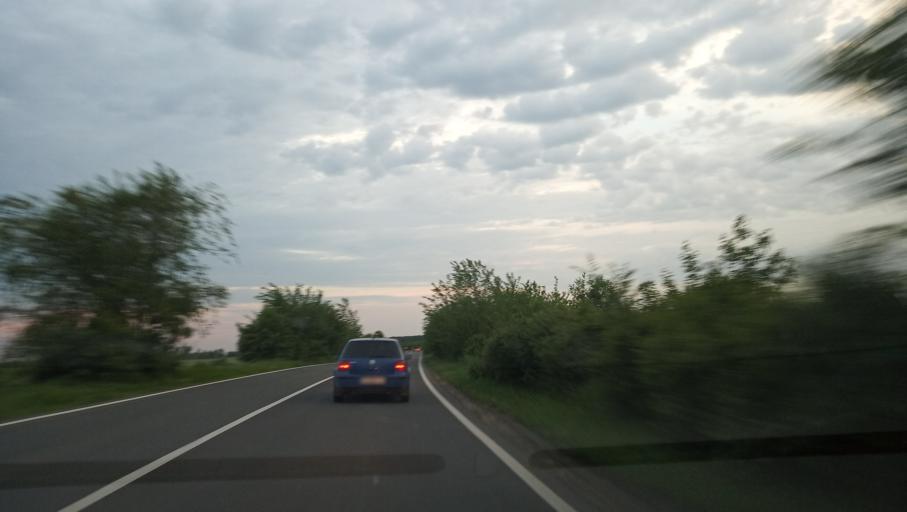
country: RO
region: Timis
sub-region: Comuna Padureni
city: Padureni
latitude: 45.6130
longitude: 21.1952
